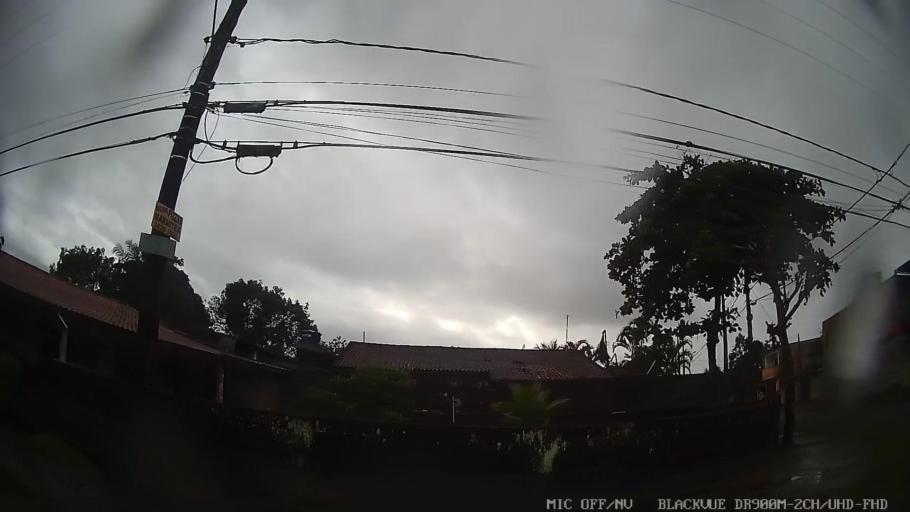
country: BR
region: Sao Paulo
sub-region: Itanhaem
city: Itanhaem
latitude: -24.2348
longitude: -46.8852
